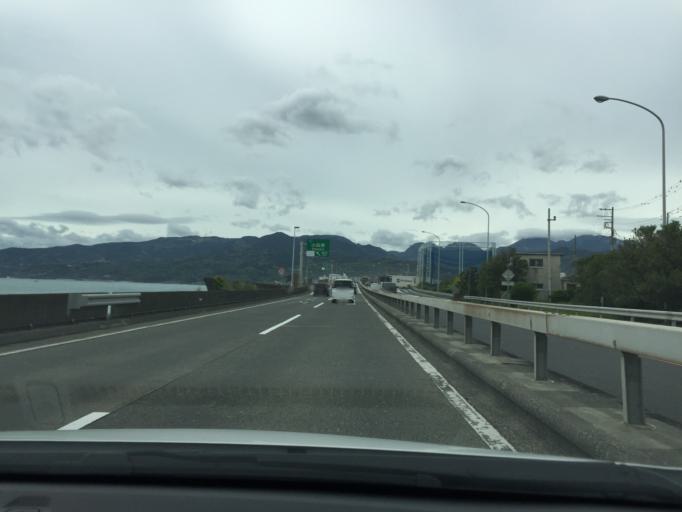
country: JP
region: Kanagawa
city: Odawara
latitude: 35.2562
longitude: 139.1746
